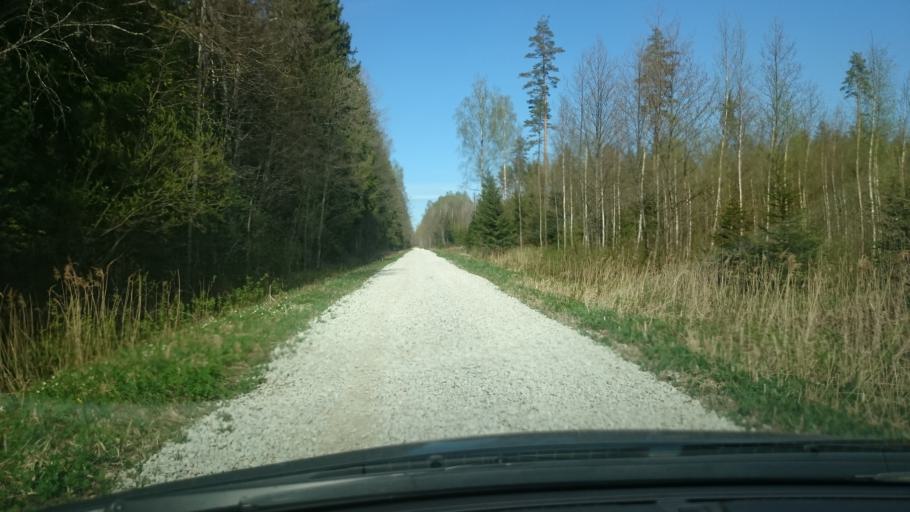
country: EE
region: Ida-Virumaa
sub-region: Sillamaee linn
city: Sillamae
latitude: 59.1659
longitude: 27.7991
